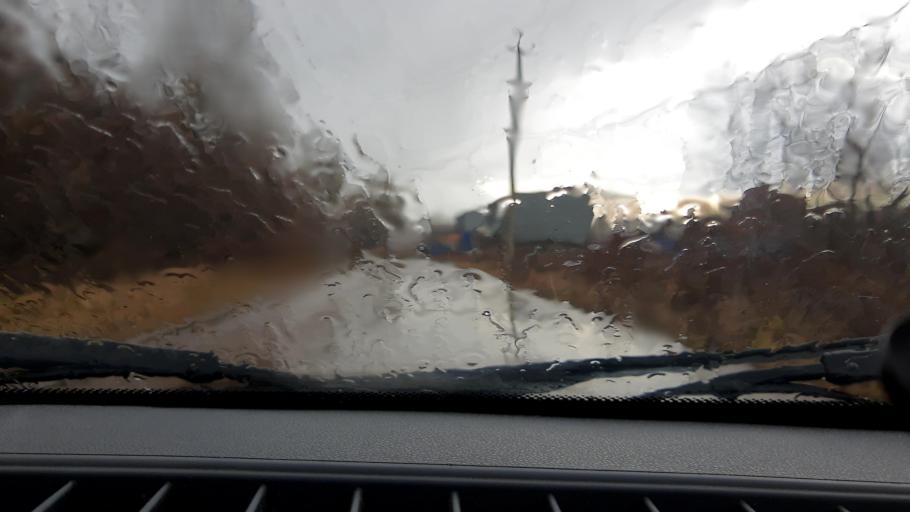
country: RU
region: Bashkortostan
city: Ufa
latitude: 54.7614
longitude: 55.9776
